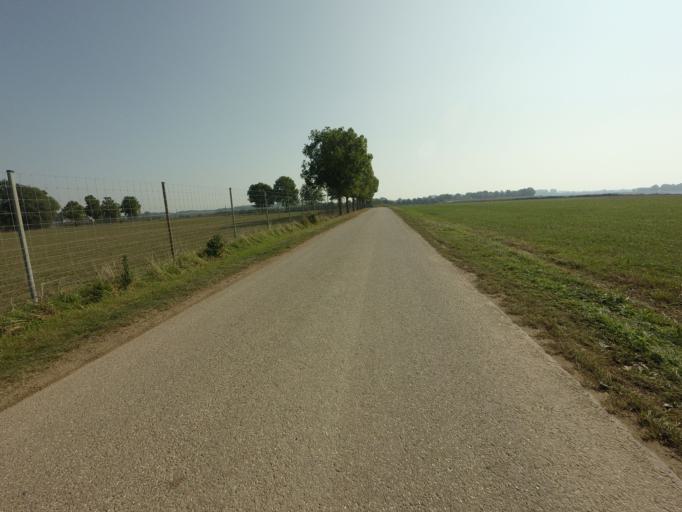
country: NL
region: Limburg
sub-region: Gemeente Roermond
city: Leeuwen
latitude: 51.2536
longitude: 5.9969
